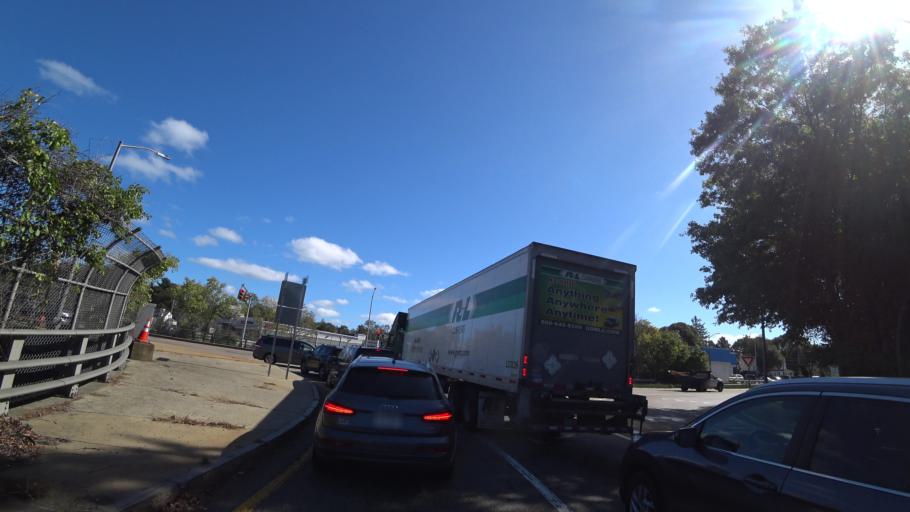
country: US
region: Massachusetts
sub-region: Norfolk County
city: Braintree
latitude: 42.2256
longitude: -71.0052
